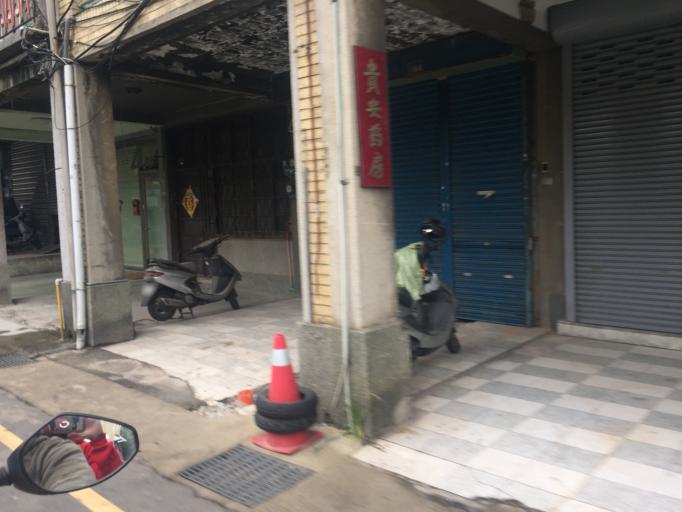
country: TW
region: Taiwan
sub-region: Hsinchu
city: Hsinchu
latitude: 24.8010
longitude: 120.9626
